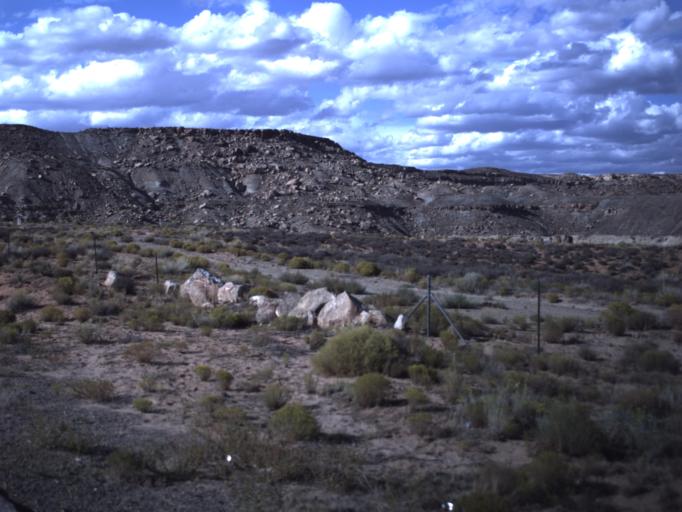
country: US
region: Utah
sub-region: San Juan County
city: Blanding
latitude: 37.3175
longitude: -109.3078
